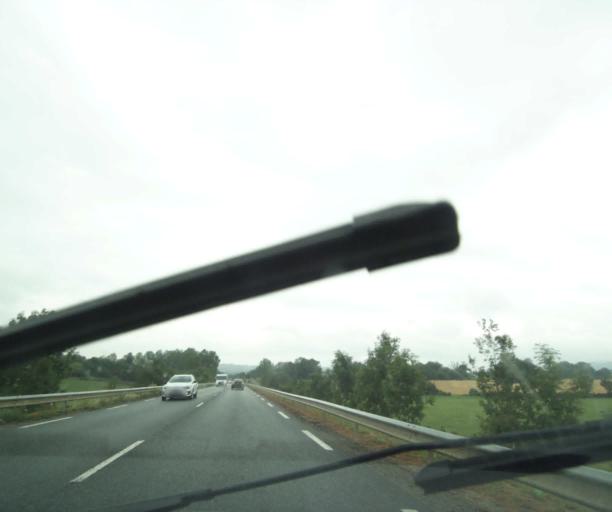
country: FR
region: Midi-Pyrenees
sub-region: Departement de l'Aveyron
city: Laissac
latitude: 44.3844
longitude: 2.8086
